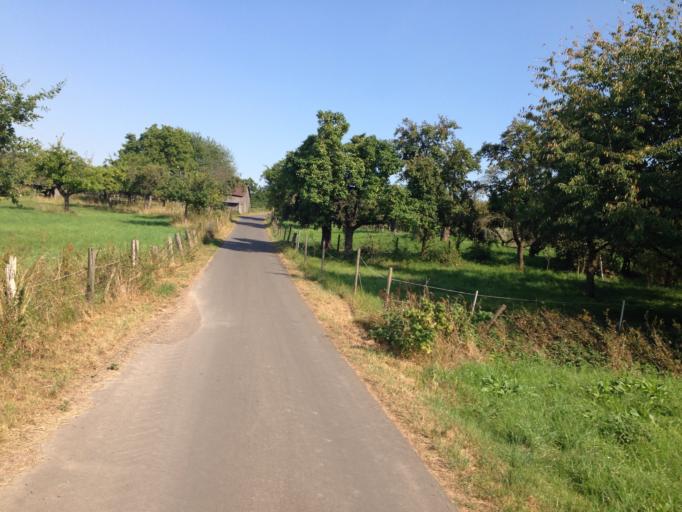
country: DE
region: Hesse
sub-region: Regierungsbezirk Giessen
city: Rabenau
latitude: 50.6720
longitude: 8.8592
